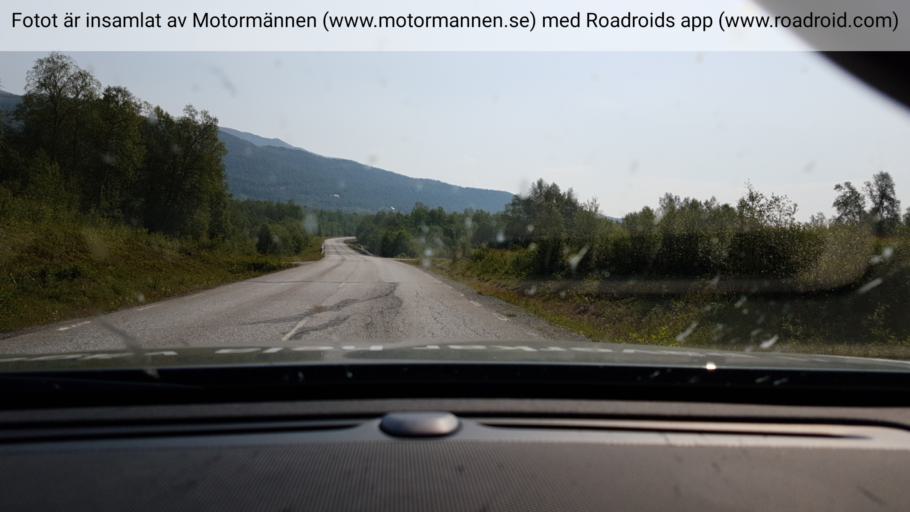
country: NO
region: Nordland
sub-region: Rana
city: Mo i Rana
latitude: 65.7819
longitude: 15.1212
